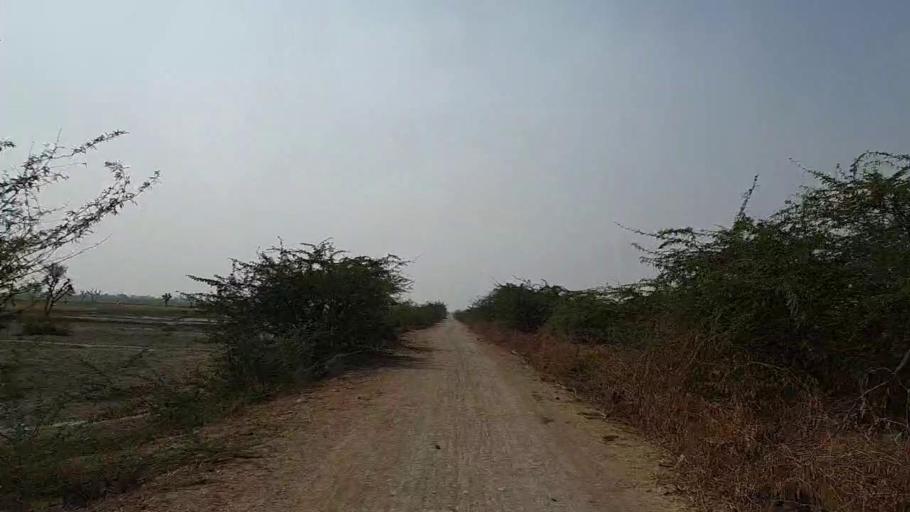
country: PK
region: Sindh
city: Naukot
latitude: 24.7605
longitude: 69.3260
